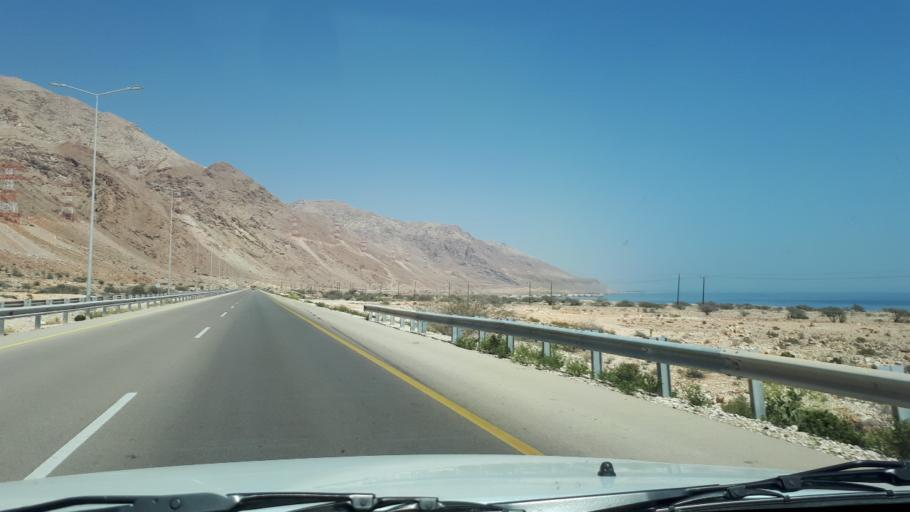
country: OM
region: Ash Sharqiyah
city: Sur
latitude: 22.7559
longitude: 59.3003
